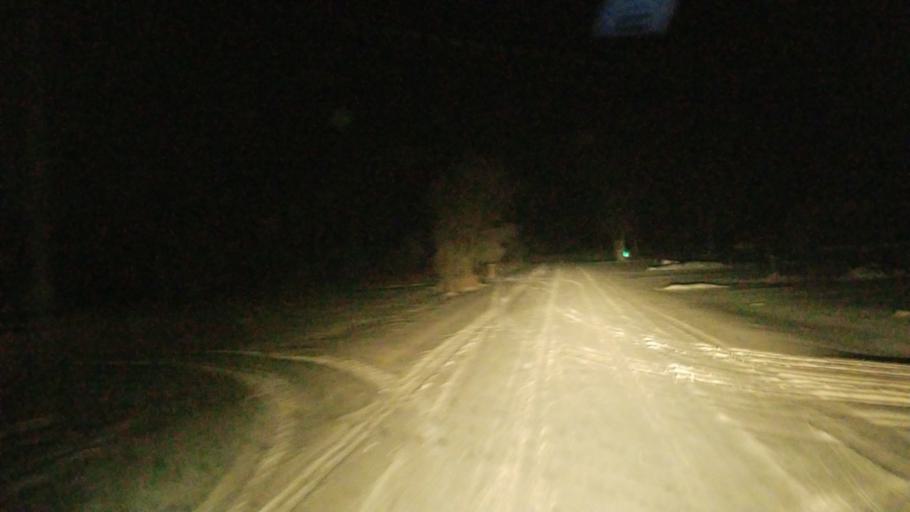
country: US
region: Michigan
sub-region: Osceola County
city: Reed City
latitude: 43.8302
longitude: -85.4141
